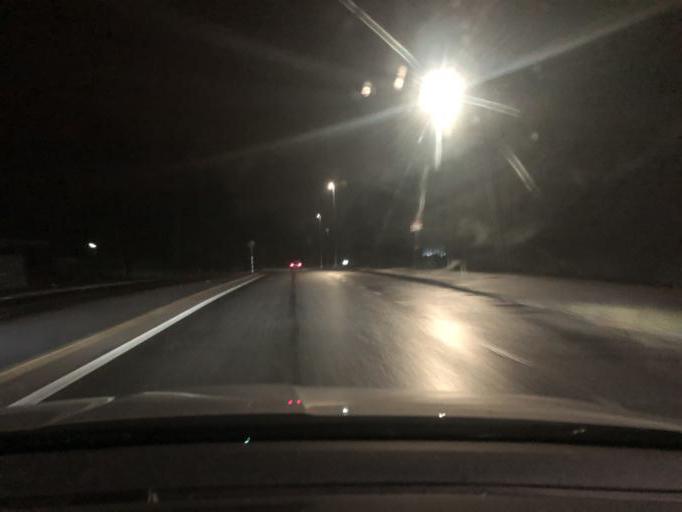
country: SE
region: Stockholm
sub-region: Jarfalla Kommun
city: Jakobsberg
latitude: 59.4656
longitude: 17.8125
